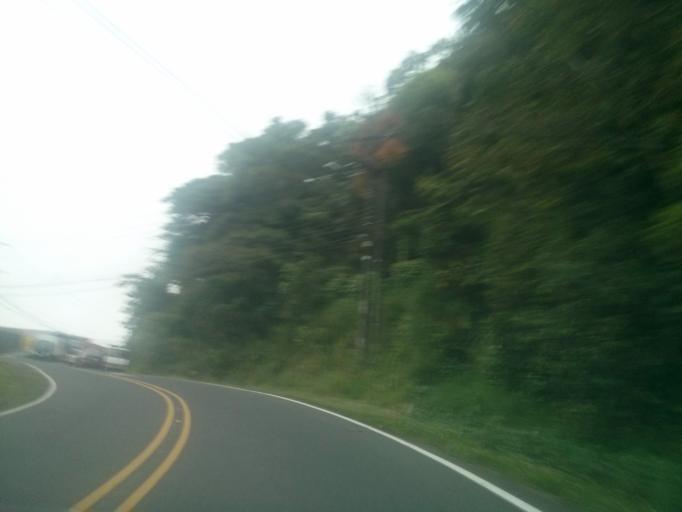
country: CR
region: Cartago
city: Cot
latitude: 9.9082
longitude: -83.8160
